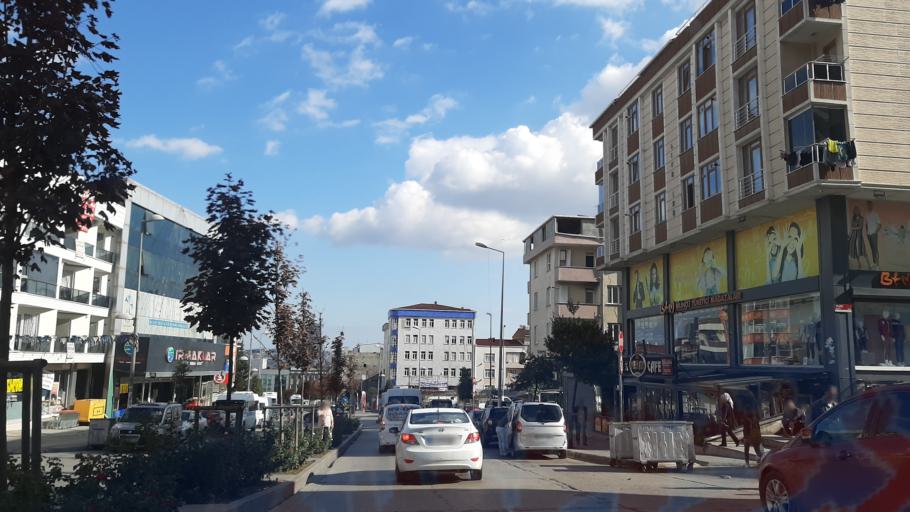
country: TR
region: Istanbul
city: Esenyurt
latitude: 41.0328
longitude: 28.6531
